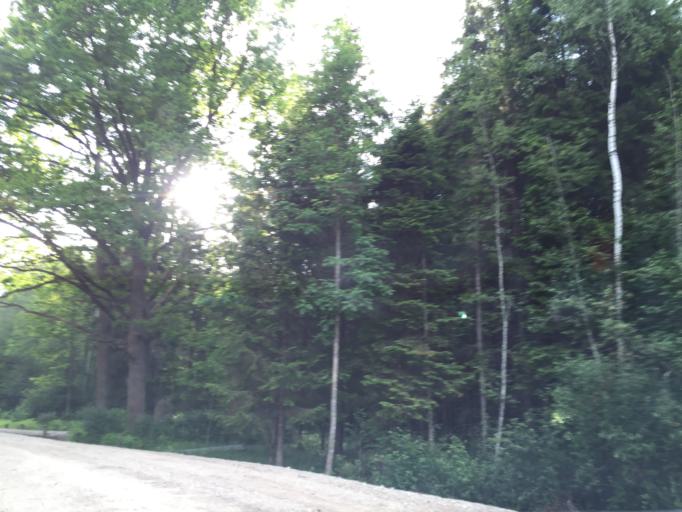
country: LV
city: Tireli
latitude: 56.7848
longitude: 23.4273
